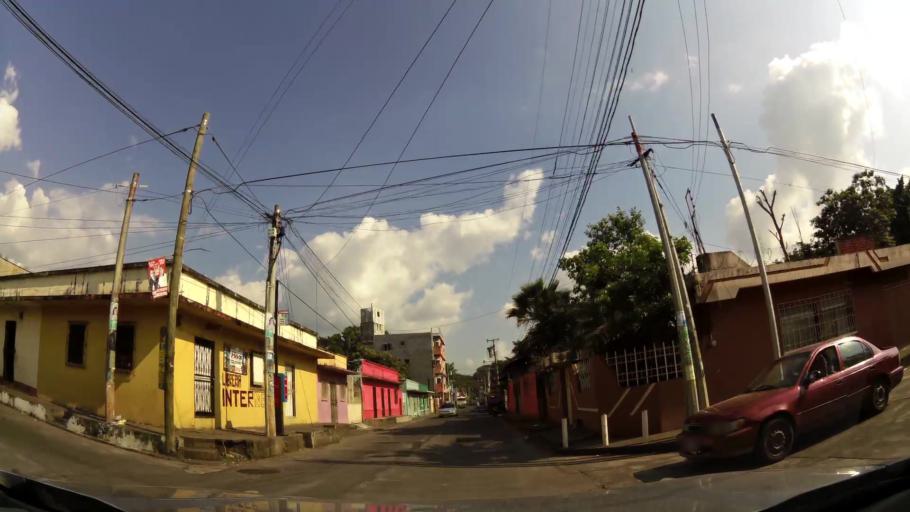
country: GT
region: Retalhuleu
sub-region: Municipio de Retalhuleu
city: Retalhuleu
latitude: 14.5389
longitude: -91.6872
